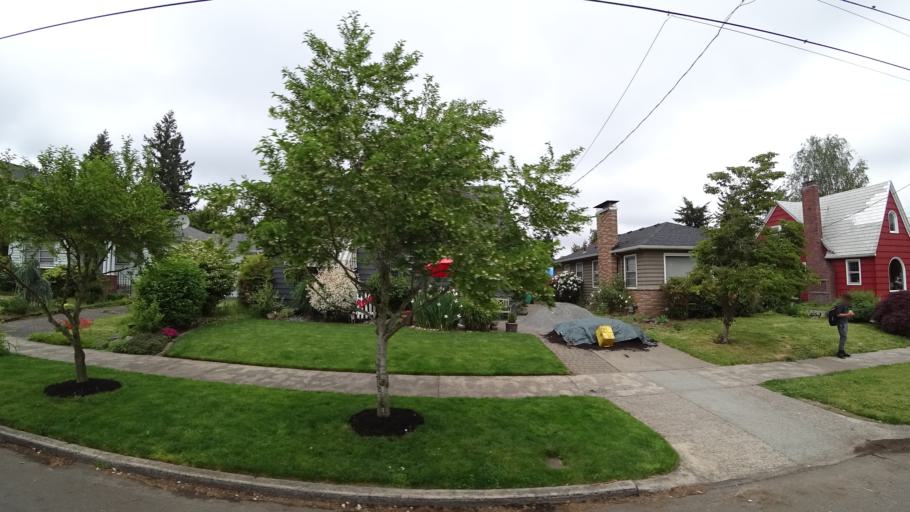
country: US
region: Oregon
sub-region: Multnomah County
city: Portland
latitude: 45.5501
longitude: -122.6174
